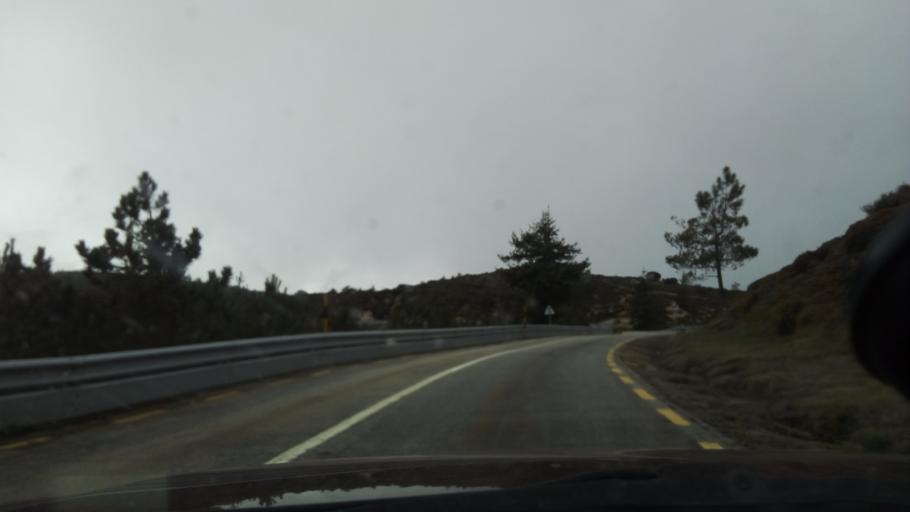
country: PT
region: Guarda
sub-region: Manteigas
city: Manteigas
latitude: 40.4161
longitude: -7.5521
